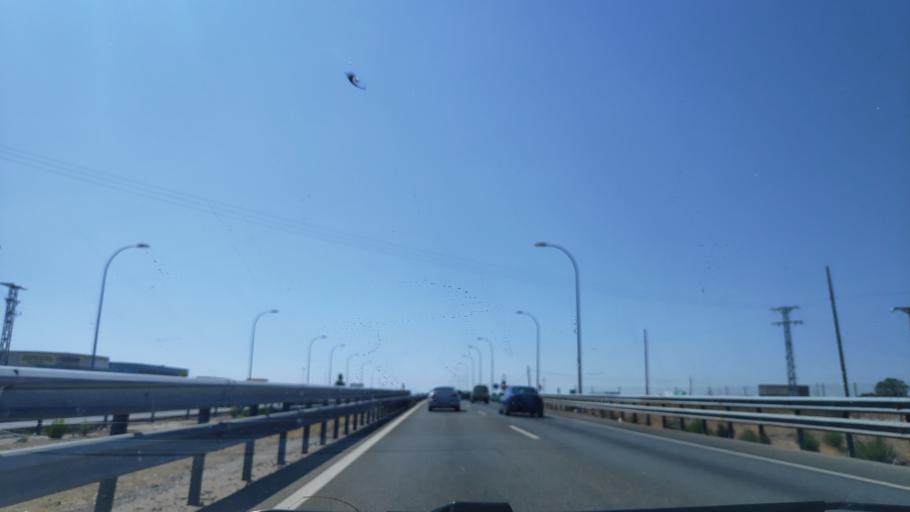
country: ES
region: Madrid
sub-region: Provincia de Madrid
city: Torrejon de la Calzada
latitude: 40.1797
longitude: -3.8095
